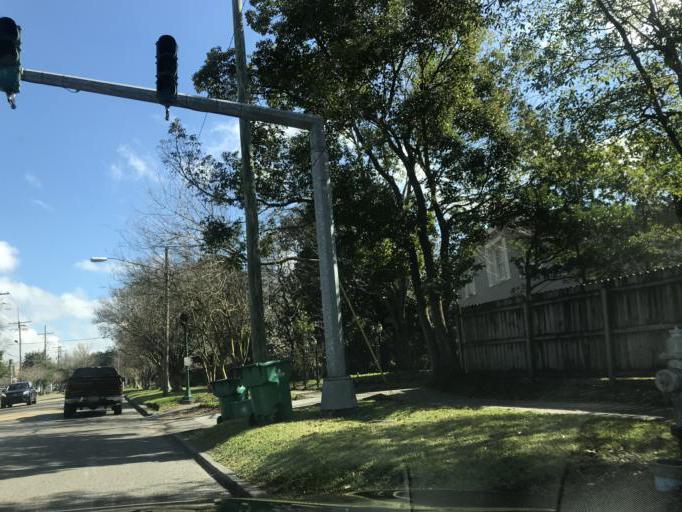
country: US
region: Louisiana
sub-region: Jefferson Parish
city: Metairie
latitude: 29.9859
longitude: -90.1435
